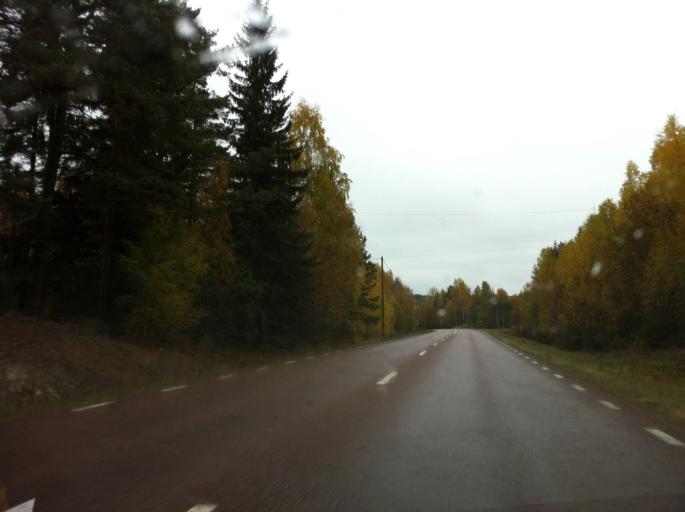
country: SE
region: Dalarna
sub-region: Ludvika Kommun
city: Grangesberg
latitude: 60.2230
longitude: 14.9737
